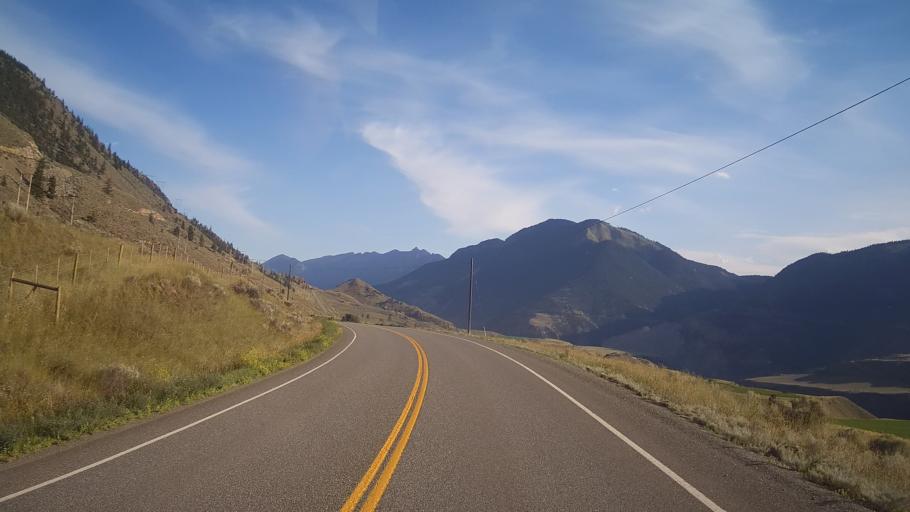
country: CA
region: British Columbia
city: Lillooet
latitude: 50.8511
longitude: -121.8621
